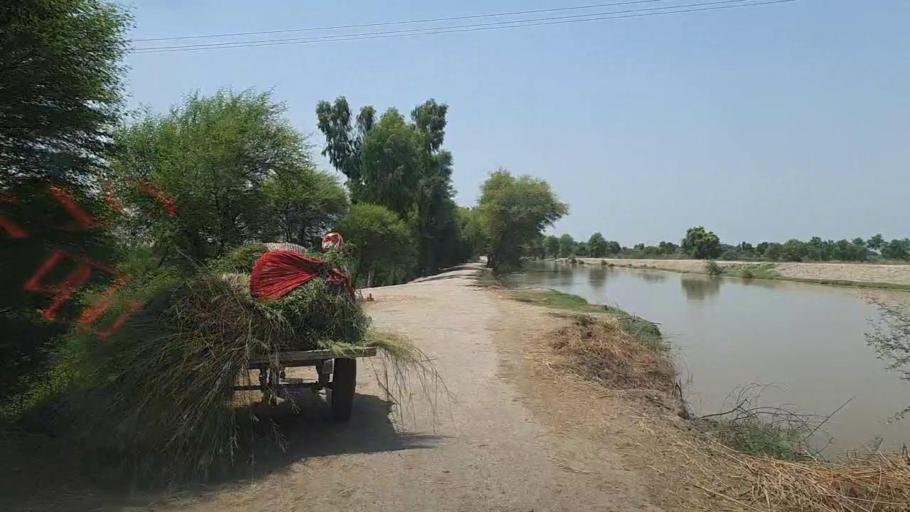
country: PK
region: Sindh
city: Ubauro
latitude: 28.1427
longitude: 69.7748
